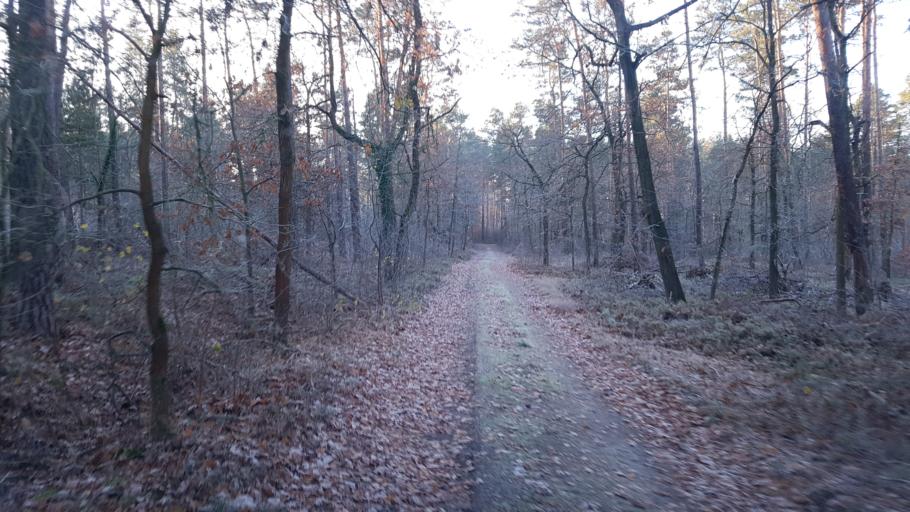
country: DE
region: Brandenburg
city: Sallgast
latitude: 51.5917
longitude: 13.8351
